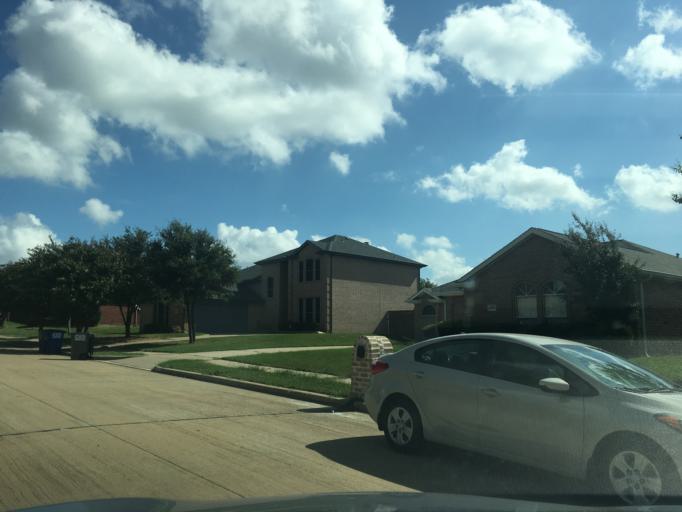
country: US
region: Texas
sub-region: Dallas County
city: Sachse
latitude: 32.9557
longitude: -96.5854
